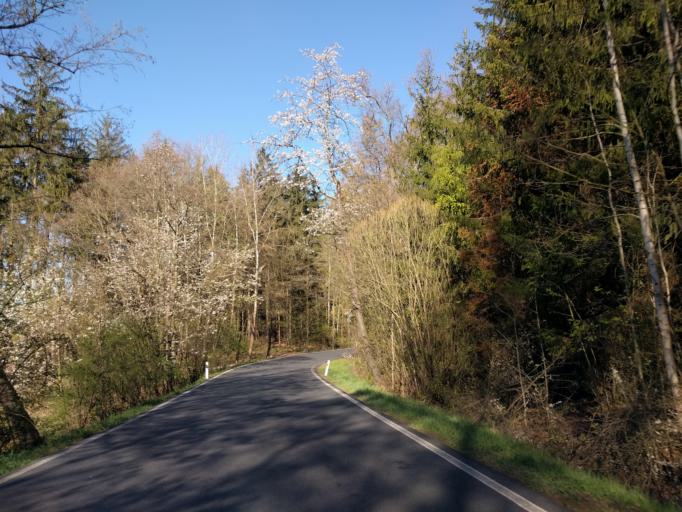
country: CZ
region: Central Bohemia
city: Ondrejov
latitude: 49.9157
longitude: 14.7559
